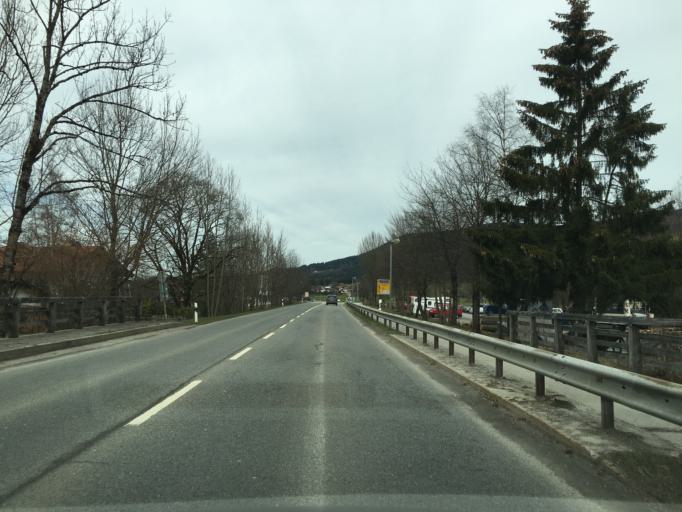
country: DE
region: Bavaria
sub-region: Upper Bavaria
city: Inzell
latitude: 47.7643
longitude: 12.7482
